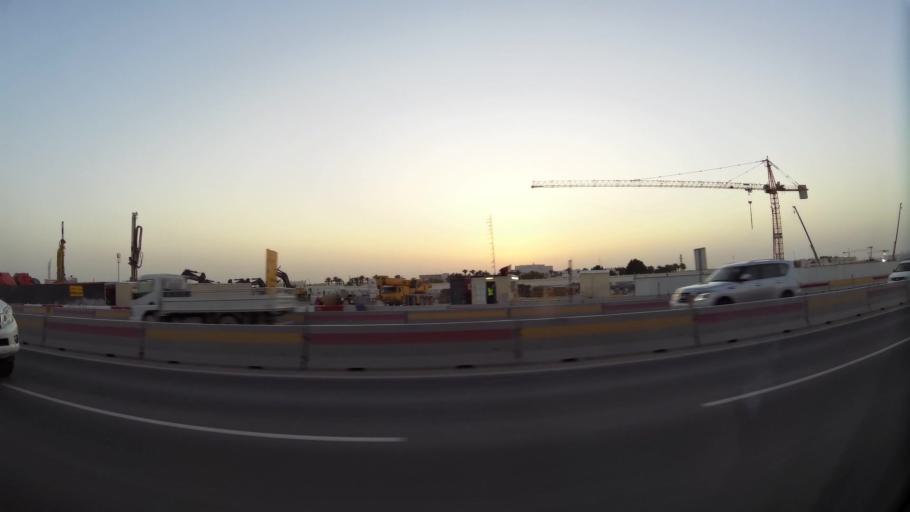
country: QA
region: Baladiyat ar Rayyan
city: Ar Rayyan
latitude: 25.2970
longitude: 51.4658
